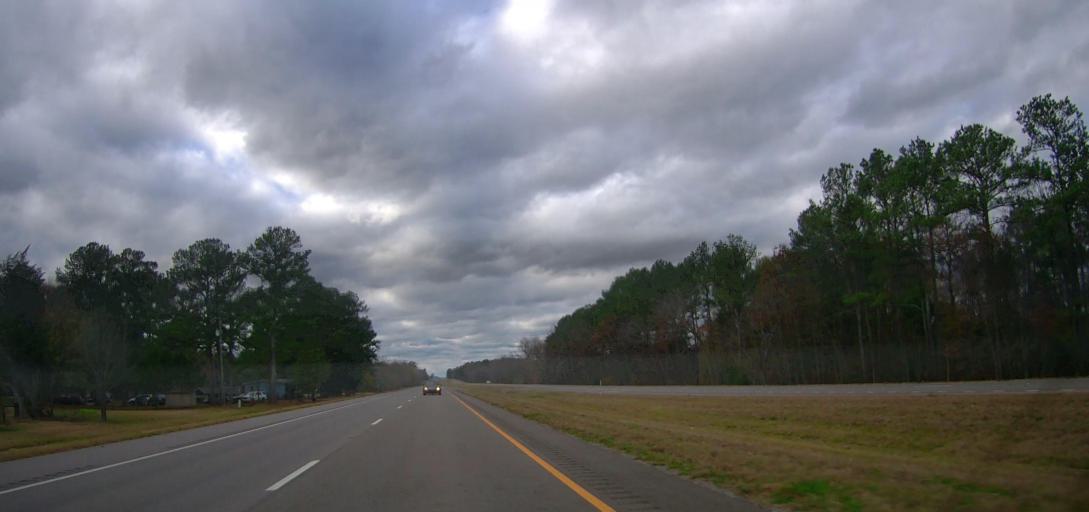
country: US
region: Alabama
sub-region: Morgan County
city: Danville
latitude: 34.3466
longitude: -87.0372
